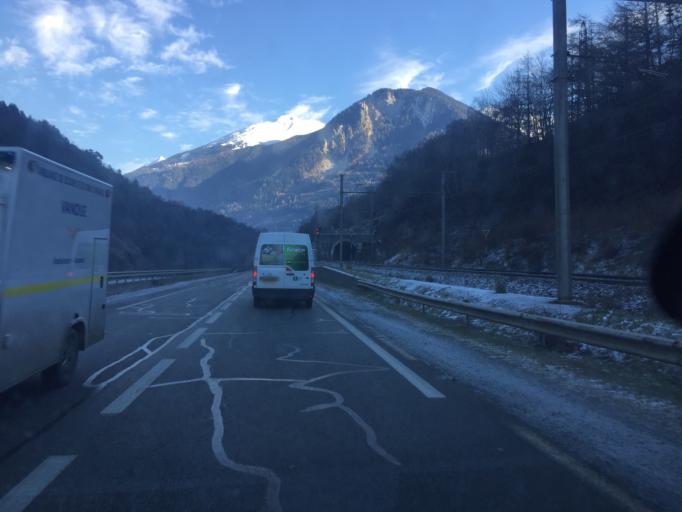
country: FR
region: Rhone-Alpes
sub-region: Departement de la Savoie
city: Modane
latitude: 45.1933
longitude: 6.6335
